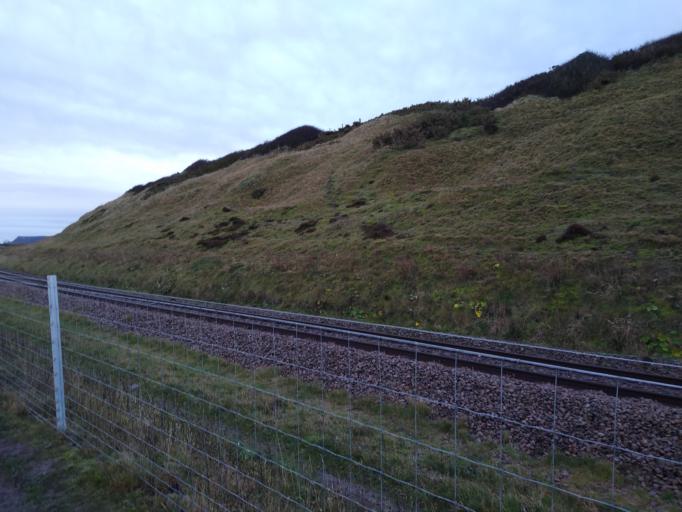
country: GB
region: England
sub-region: Redcar and Cleveland
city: Saltburn-by-the-Sea
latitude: 54.5860
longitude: -0.9285
